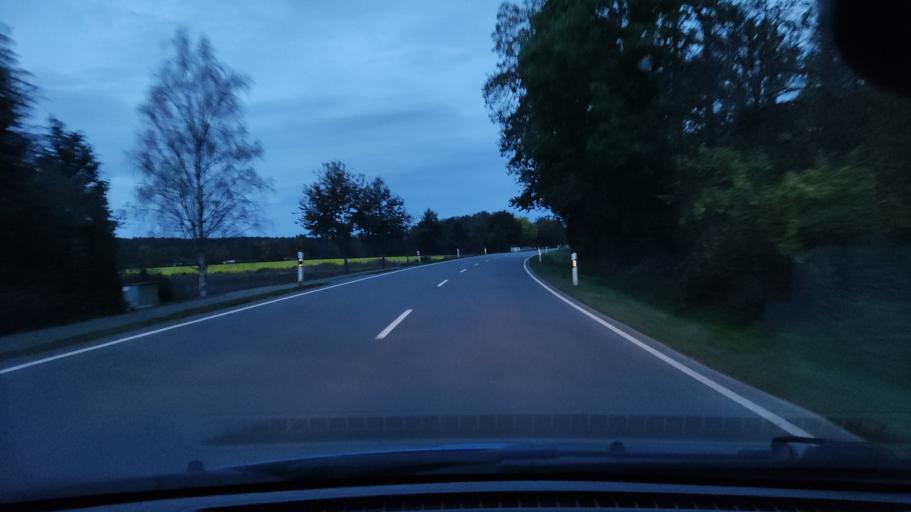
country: DE
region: Lower Saxony
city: Woltersdorf
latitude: 52.9631
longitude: 11.2542
